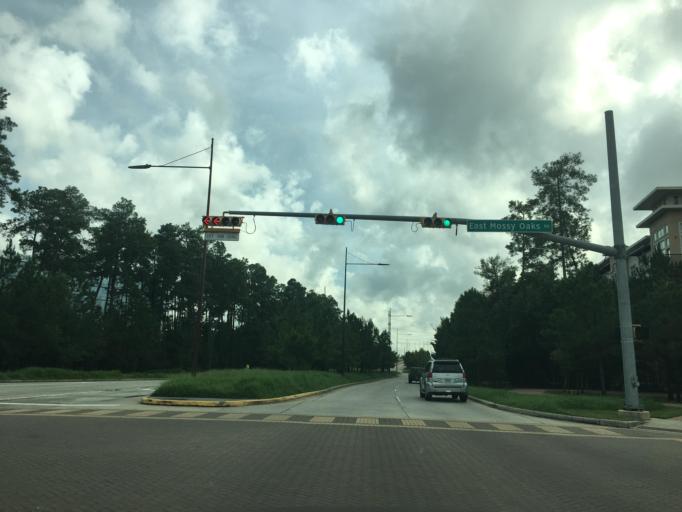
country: US
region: Texas
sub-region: Harris County
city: Spring
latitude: 30.0925
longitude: -95.4499
